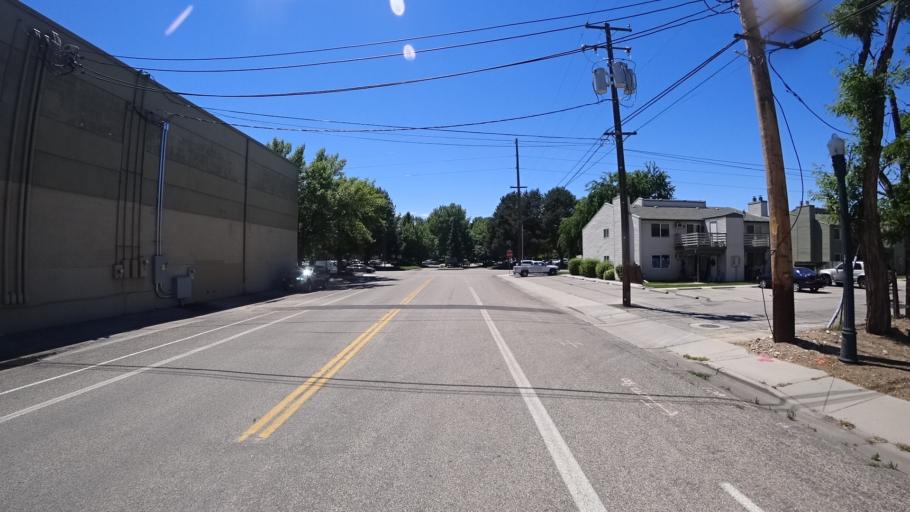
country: US
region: Idaho
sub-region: Ada County
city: Boise
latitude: 43.6128
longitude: -116.2115
